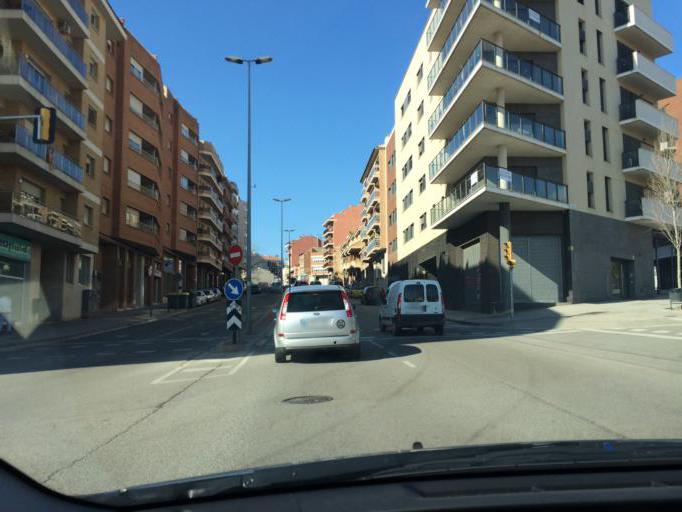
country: ES
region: Catalonia
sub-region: Provincia de Barcelona
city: Manresa
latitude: 41.7352
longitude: 1.8350
